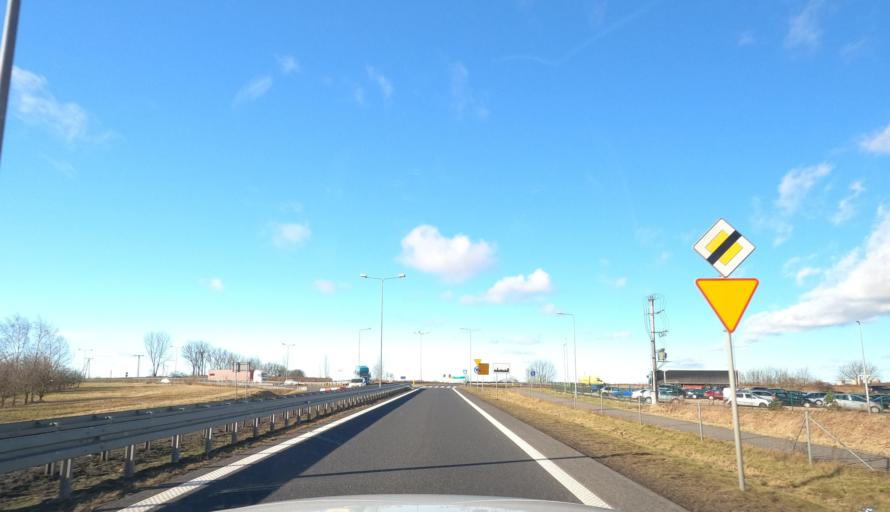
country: PL
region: West Pomeranian Voivodeship
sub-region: Powiat stargardzki
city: Stargard Szczecinski
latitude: 53.3083
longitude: 15.0255
